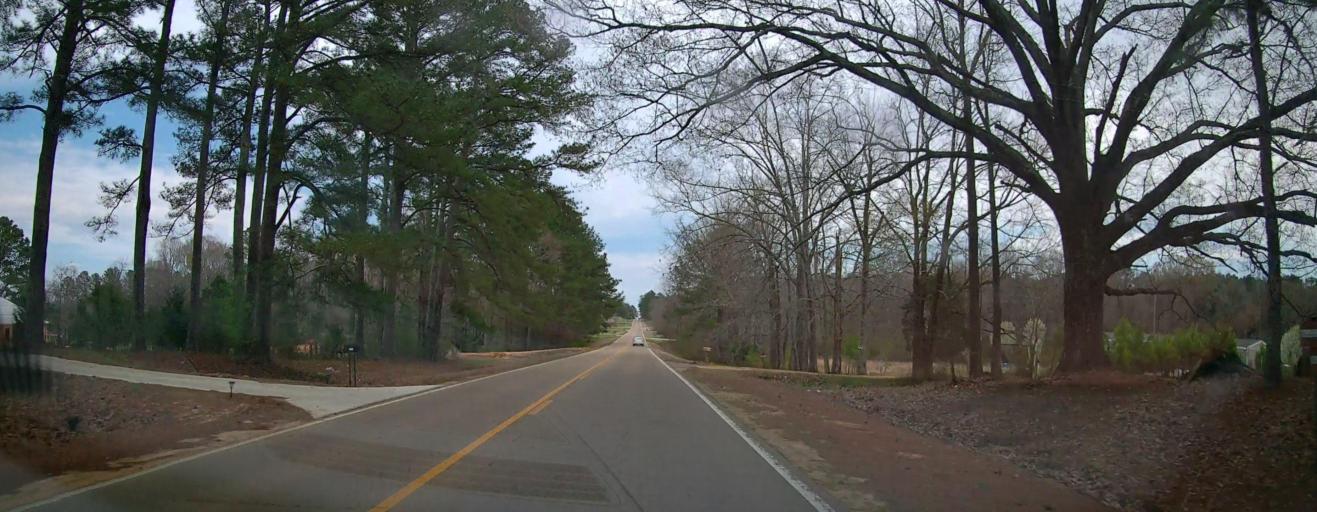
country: US
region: Mississippi
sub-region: Itawamba County
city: Mantachie
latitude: 34.2658
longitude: -88.5503
